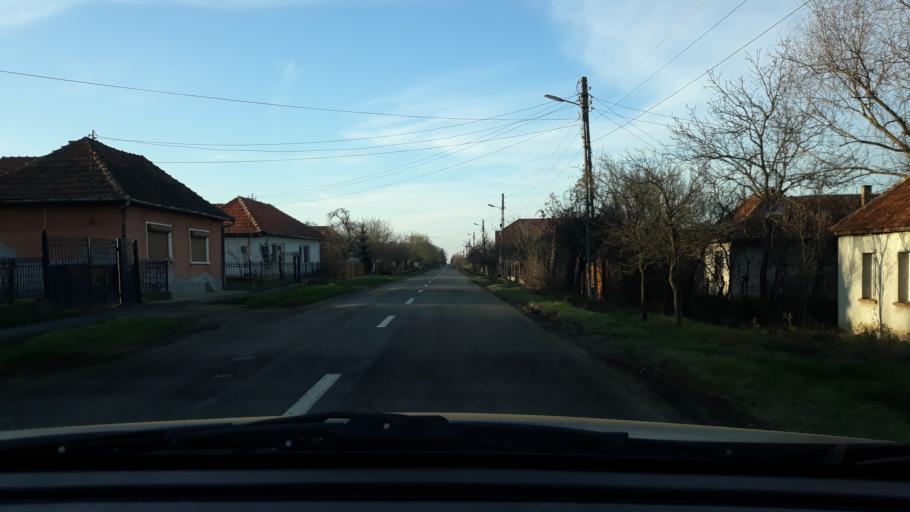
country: RO
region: Bihor
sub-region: Comuna Balc
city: Balc
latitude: 47.2765
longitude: 22.4826
